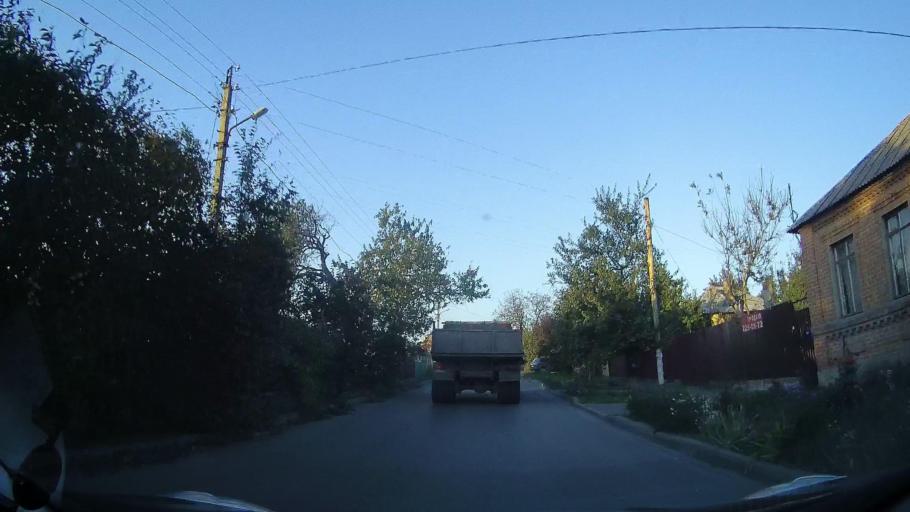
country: RU
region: Rostov
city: Rostov-na-Donu
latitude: 47.2511
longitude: 39.6838
